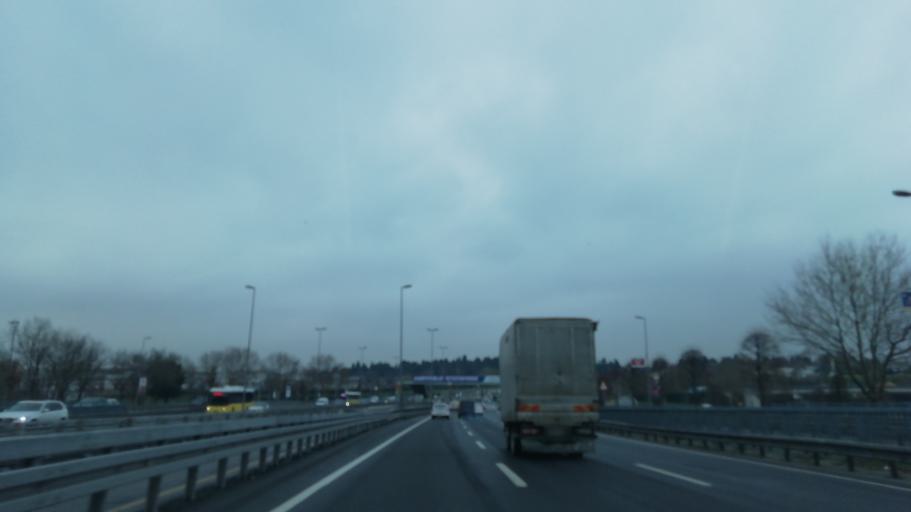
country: TR
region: Istanbul
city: Istanbul
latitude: 41.0285
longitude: 28.9240
